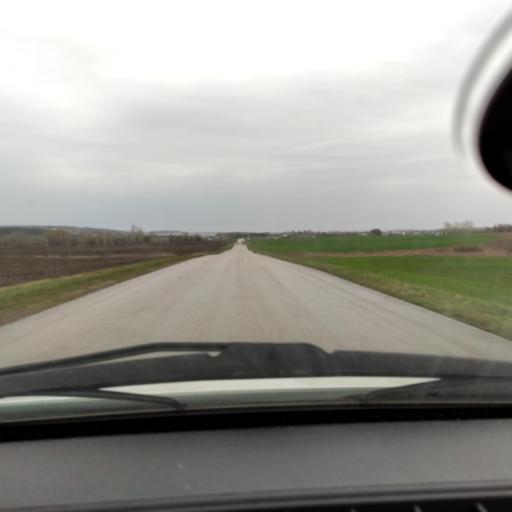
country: RU
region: Bashkortostan
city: Tolbazy
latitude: 54.1701
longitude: 55.9347
